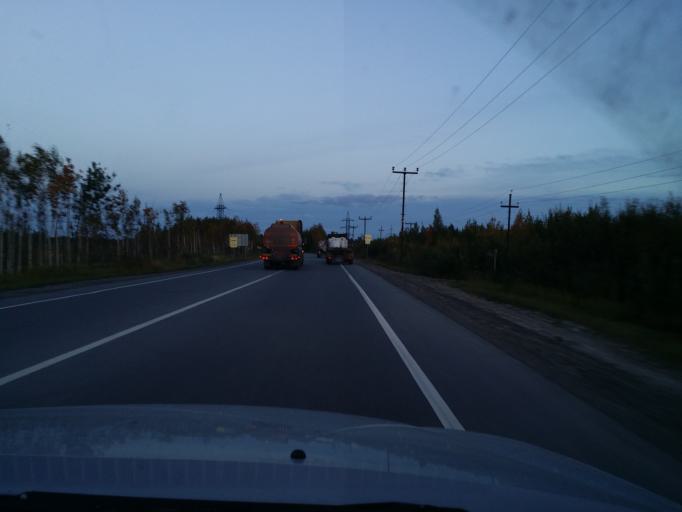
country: RU
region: Khanty-Mansiyskiy Avtonomnyy Okrug
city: Nizhnevartovsk
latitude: 61.0298
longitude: 76.3623
